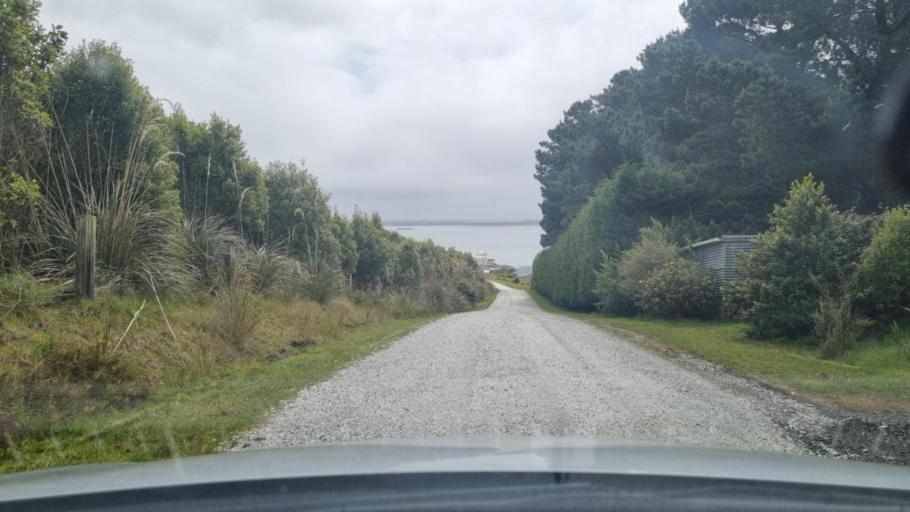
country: NZ
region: Southland
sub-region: Invercargill City
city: Bluff
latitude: -46.6103
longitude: 168.3522
